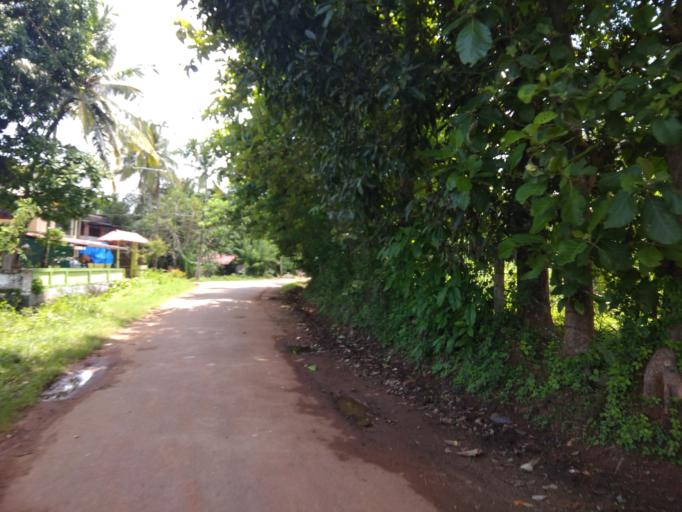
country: IN
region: Kerala
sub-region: Thrissur District
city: Trichur
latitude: 10.5421
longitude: 76.1698
